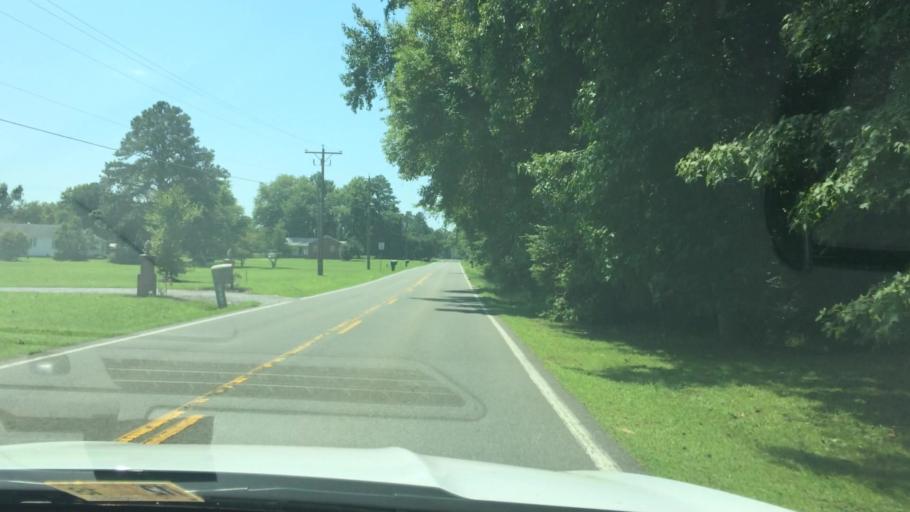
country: US
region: Virginia
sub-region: Charles City County
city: Charles City
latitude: 37.3945
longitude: -77.0504
